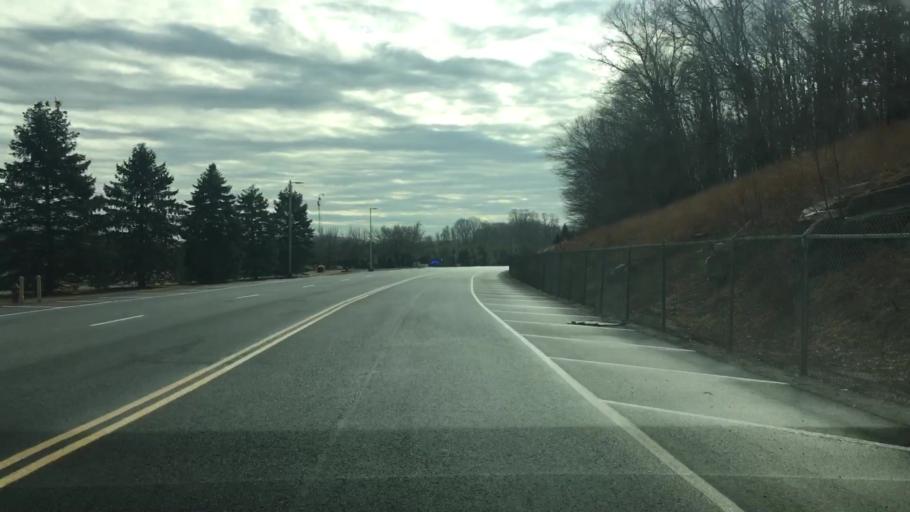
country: US
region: Connecticut
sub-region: Middlesex County
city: Higganum
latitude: 41.5364
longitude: -72.5616
